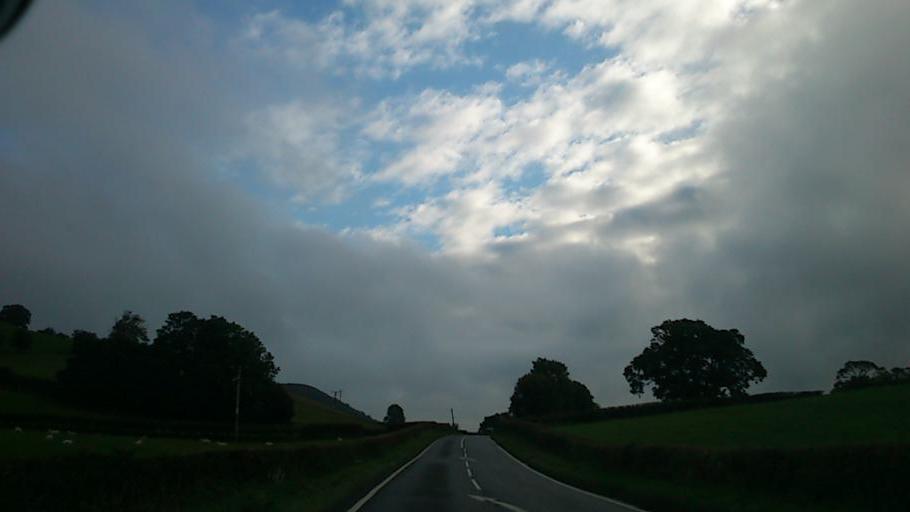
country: GB
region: Wales
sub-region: Sir Powys
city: Welshpool
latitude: 52.6504
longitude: -3.2341
